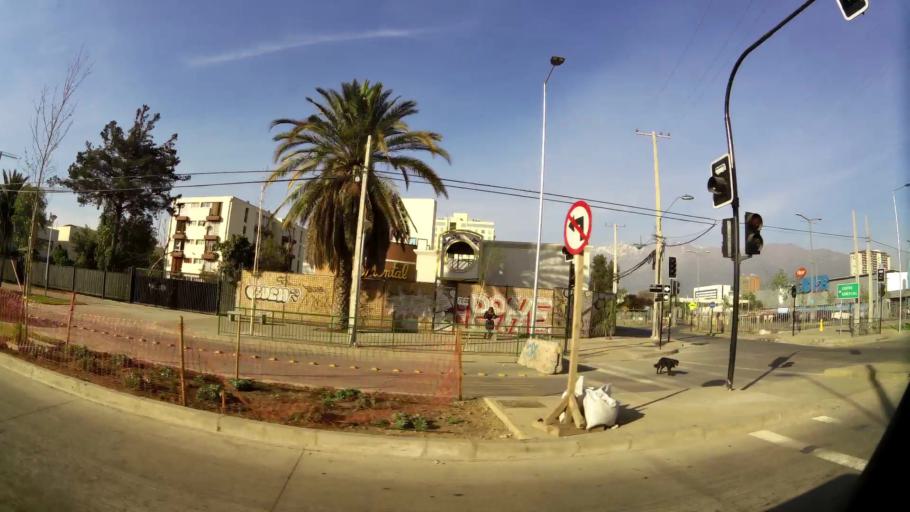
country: CL
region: Santiago Metropolitan
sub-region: Provincia de Santiago
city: Villa Presidente Frei, Nunoa, Santiago, Chile
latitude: -33.5188
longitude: -70.6036
